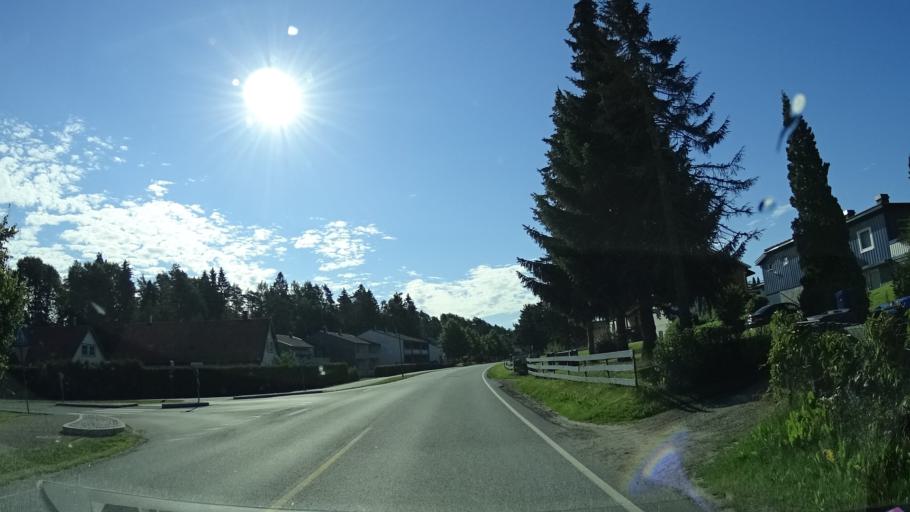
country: NO
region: Ostfold
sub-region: Eidsberg
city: Mysen
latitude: 59.5515
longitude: 11.3414
